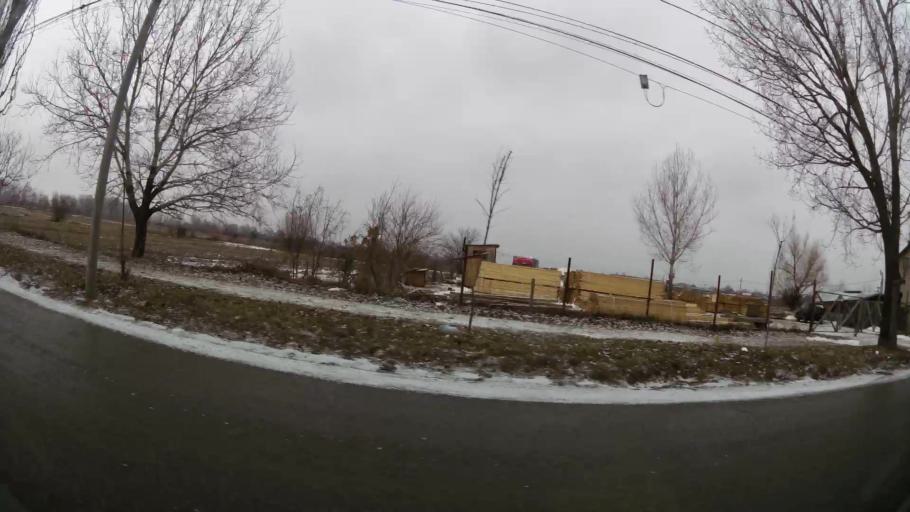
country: RO
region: Dambovita
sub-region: Municipiul Targoviste
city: Targoviste
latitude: 44.9217
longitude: 25.4829
